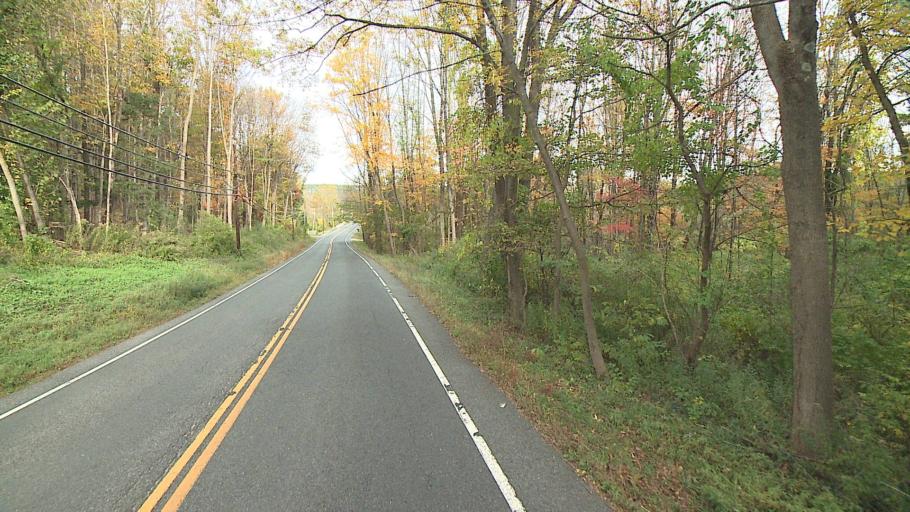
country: US
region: Connecticut
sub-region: Litchfield County
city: Canaan
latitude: 42.0230
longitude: -73.3437
